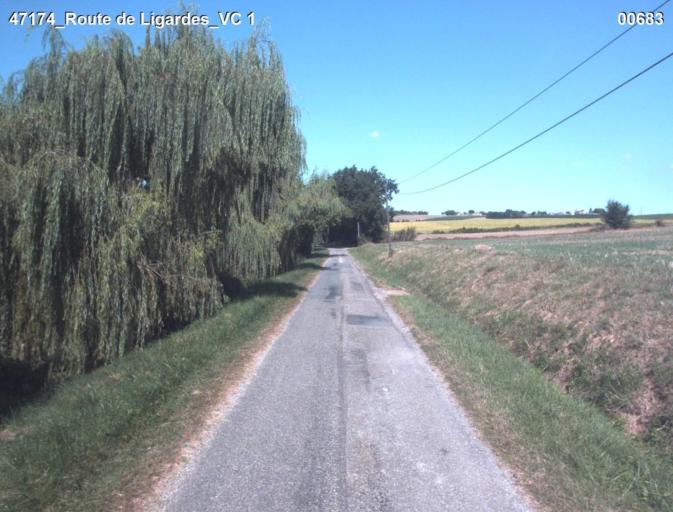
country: FR
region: Midi-Pyrenees
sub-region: Departement du Gers
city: Condom
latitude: 44.0306
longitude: 0.4109
